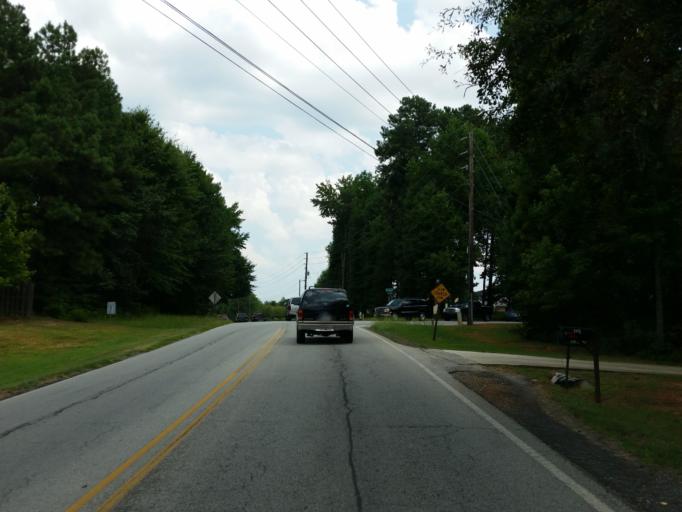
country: US
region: Georgia
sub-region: Henry County
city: Stockbridge
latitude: 33.4830
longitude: -84.2304
